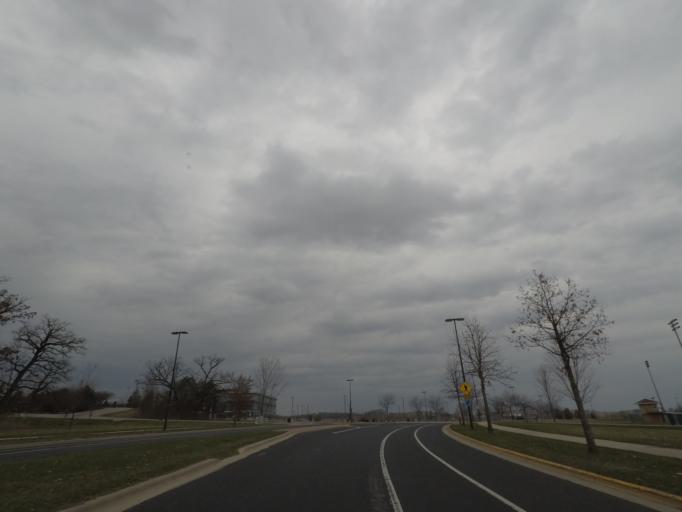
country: US
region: Wisconsin
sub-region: Dane County
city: Middleton
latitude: 43.1090
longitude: -89.5375
